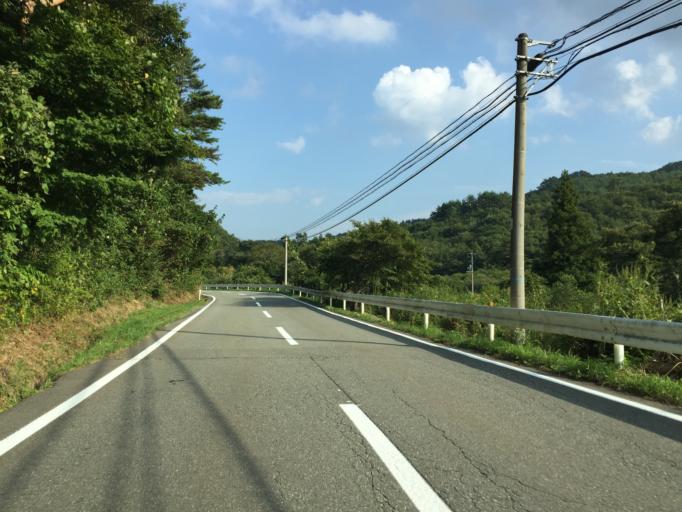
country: JP
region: Fukushima
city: Funehikimachi-funehiki
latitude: 37.5566
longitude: 140.7754
